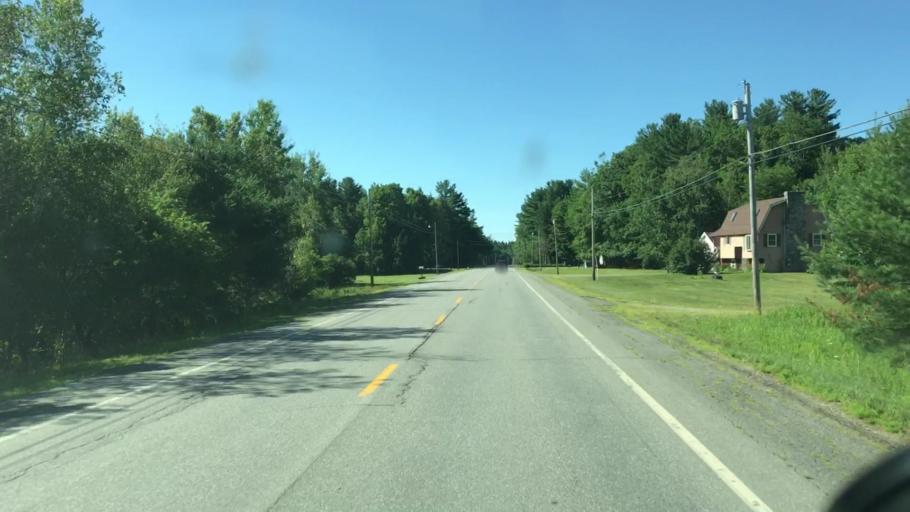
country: US
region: Maine
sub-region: Penobscot County
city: Howland
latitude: 45.2628
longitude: -68.6383
